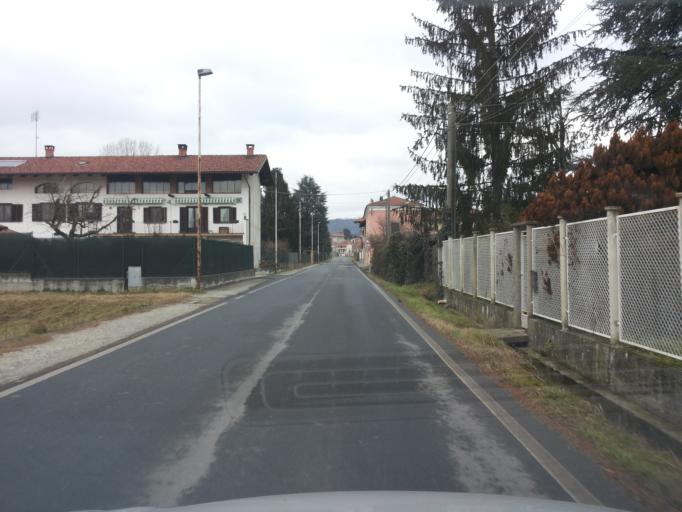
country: IT
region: Piedmont
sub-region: Provincia di Torino
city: Borgomasino
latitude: 45.3554
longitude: 7.9895
